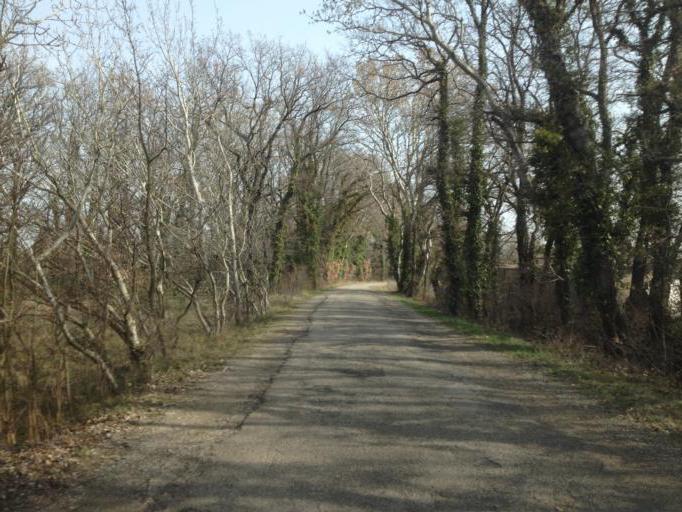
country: FR
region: Provence-Alpes-Cote d'Azur
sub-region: Departement du Vaucluse
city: Courthezon
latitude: 44.0831
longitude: 4.9212
